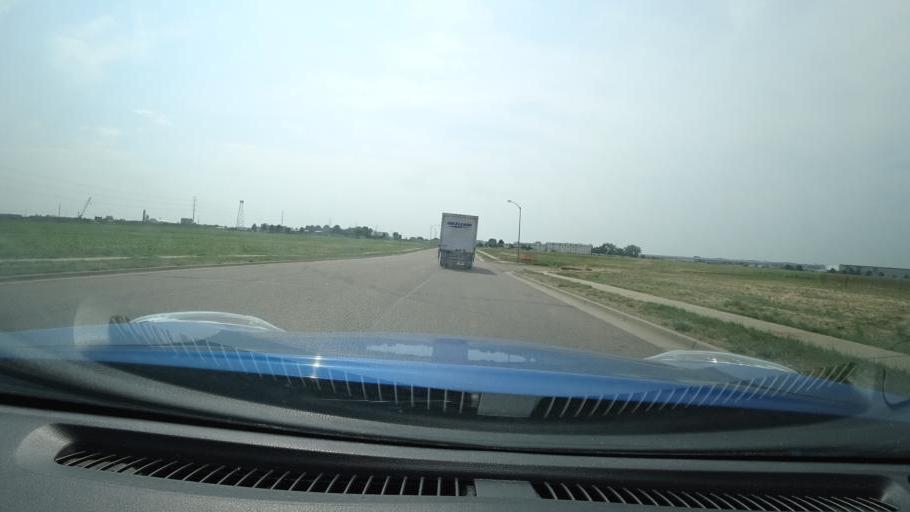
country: US
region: Colorado
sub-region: Adams County
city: Aurora
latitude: 39.7568
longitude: -104.7353
